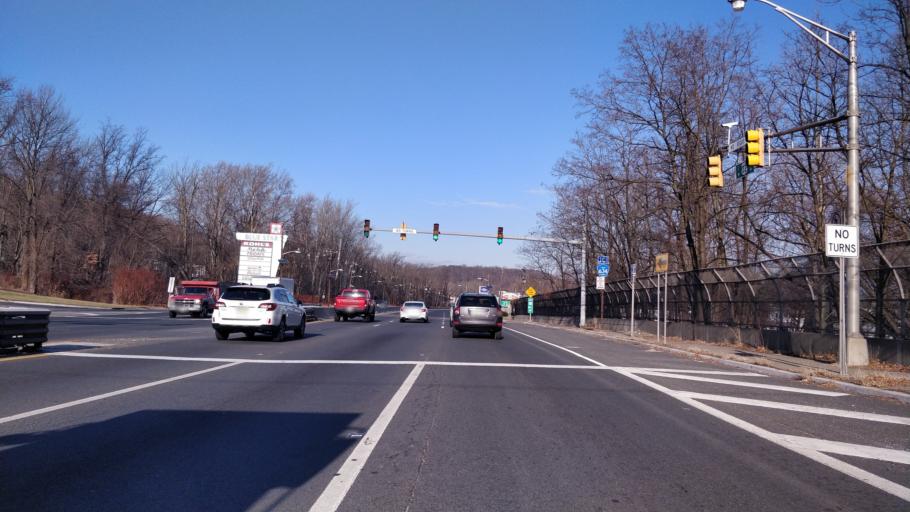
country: US
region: New Jersey
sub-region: Union County
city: Plainfield
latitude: 40.6486
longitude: -74.4069
